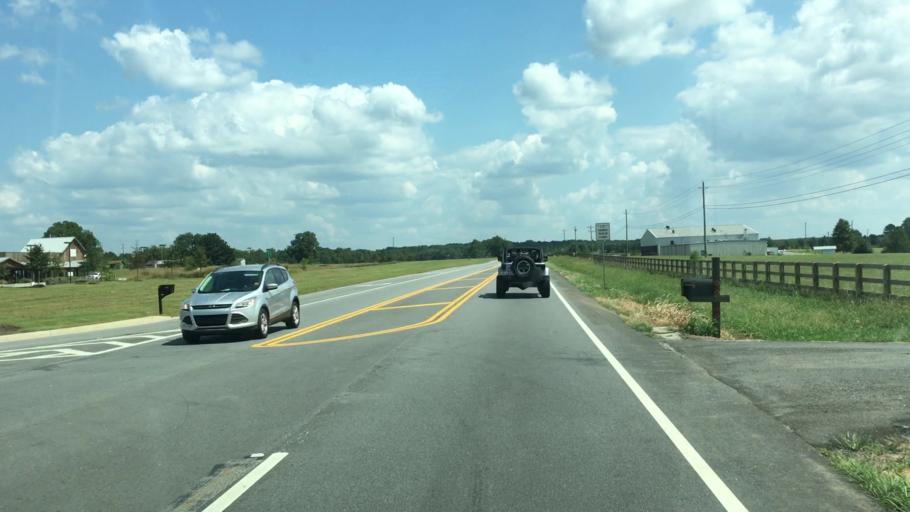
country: US
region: Georgia
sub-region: Morgan County
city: Madison
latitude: 33.5403
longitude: -83.4633
